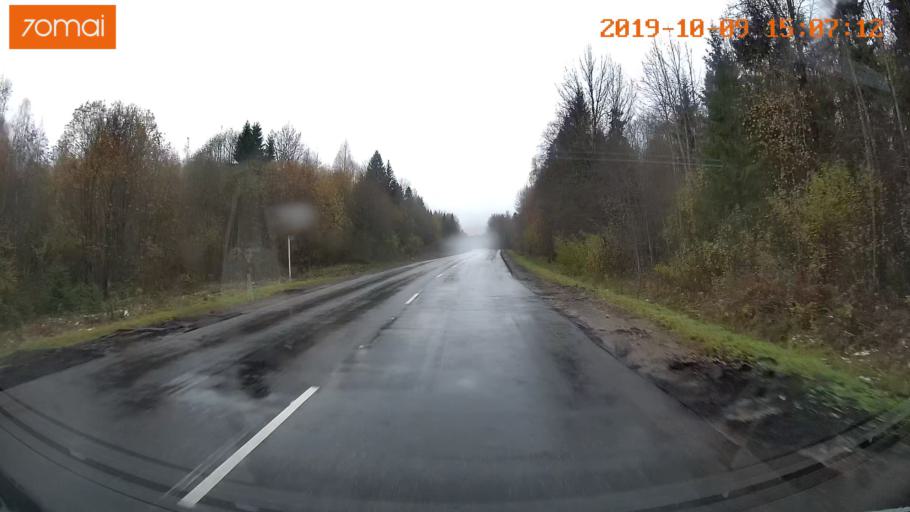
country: RU
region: Kostroma
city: Susanino
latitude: 58.2223
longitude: 41.6526
